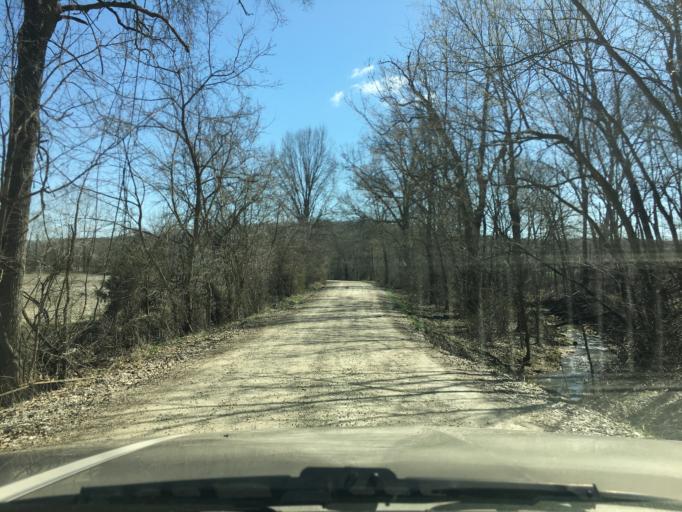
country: US
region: Missouri
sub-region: Franklin County
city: New Haven
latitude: 38.5532
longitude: -91.3285
